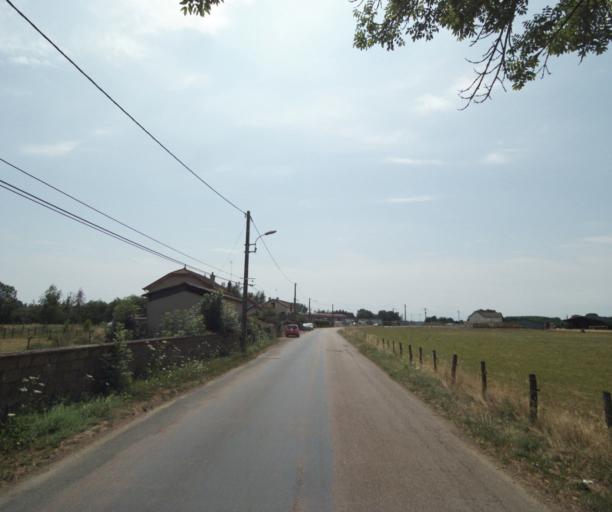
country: FR
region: Bourgogne
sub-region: Departement de Saone-et-Loire
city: Gueugnon
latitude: 46.5903
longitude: 4.0537
